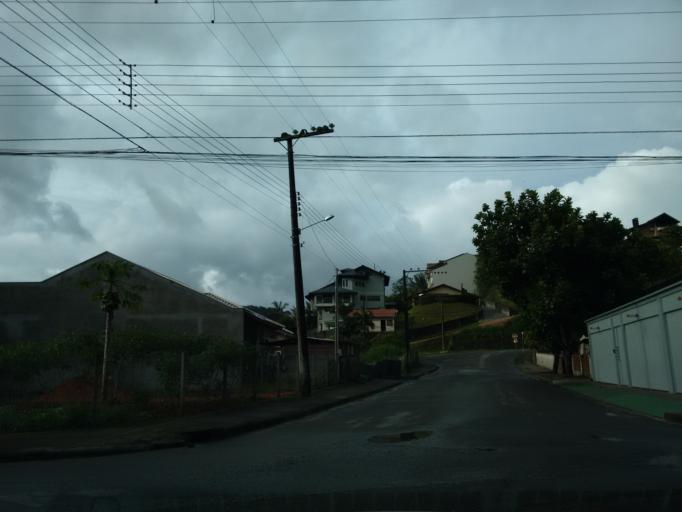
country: BR
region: Santa Catarina
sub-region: Pomerode
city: Pomerode
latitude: -26.7270
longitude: -49.1688
